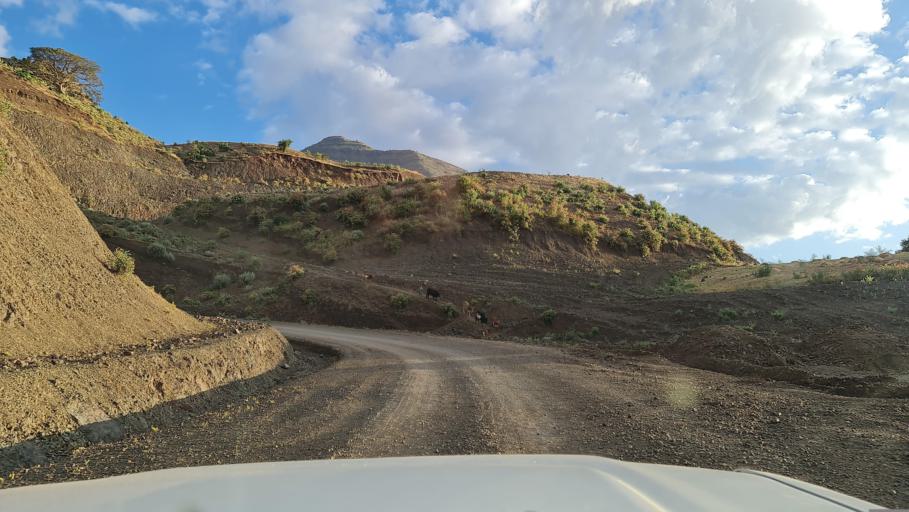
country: ET
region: Amhara
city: Debark'
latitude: 13.0272
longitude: 38.0524
